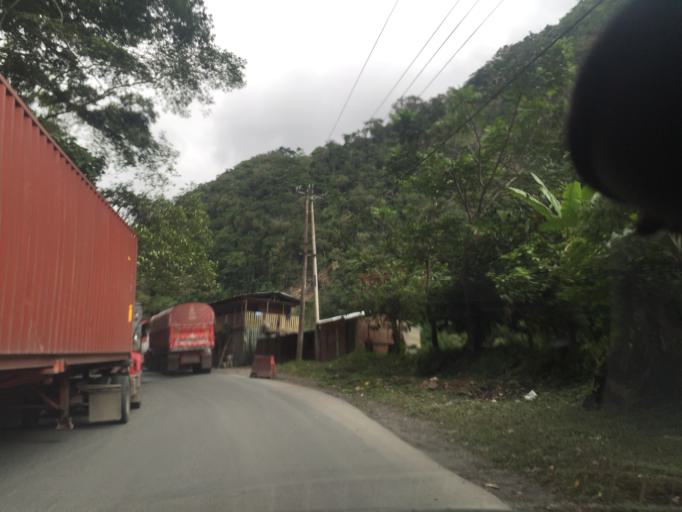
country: CO
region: Valle del Cauca
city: Dagua
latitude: 3.7767
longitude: -76.7521
